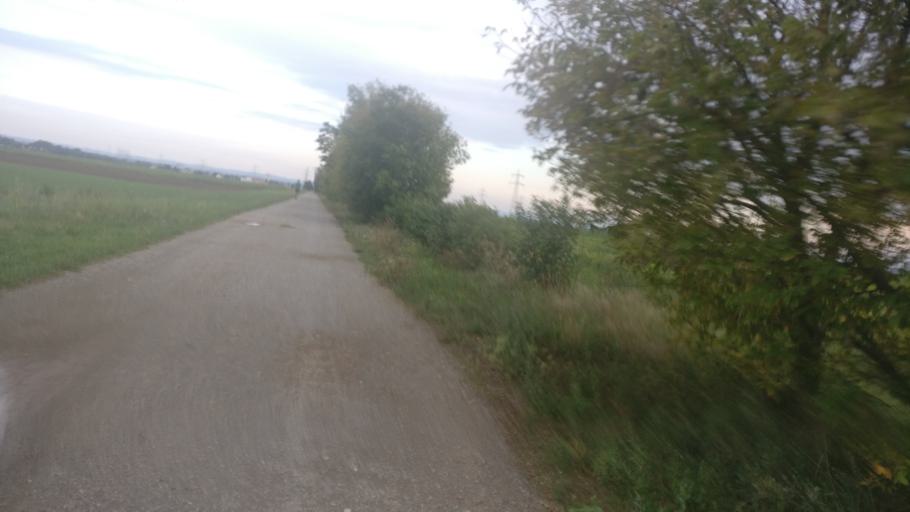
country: AT
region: Lower Austria
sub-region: Politischer Bezirk Wien-Umgebung
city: Lanzendorf
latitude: 48.1203
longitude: 16.4339
